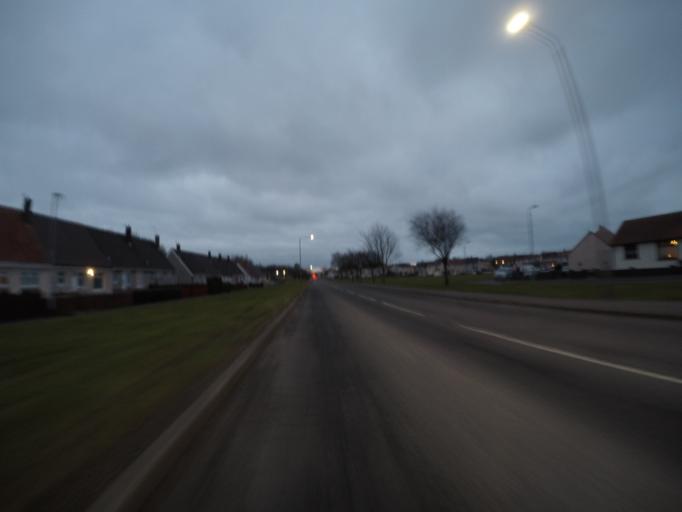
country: GB
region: Scotland
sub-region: North Ayrshire
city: Kilwinning
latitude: 55.6505
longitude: -4.6990
